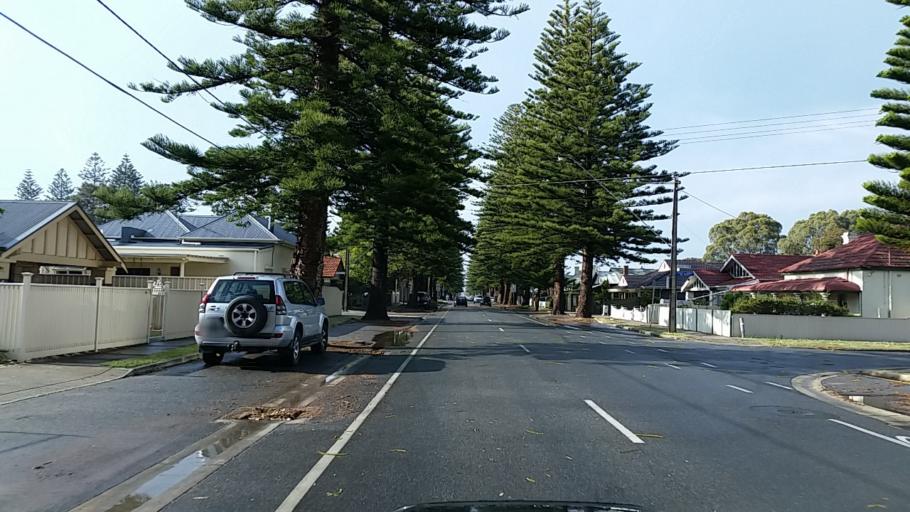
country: AU
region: South Australia
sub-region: Charles Sturt
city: Henley Beach
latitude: -34.9210
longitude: 138.4973
